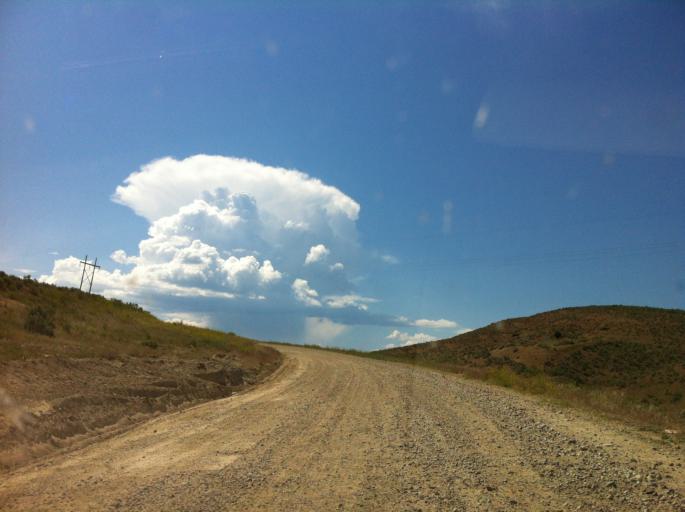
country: US
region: Oregon
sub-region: Baker County
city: Baker City
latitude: 44.7061
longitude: -117.7838
